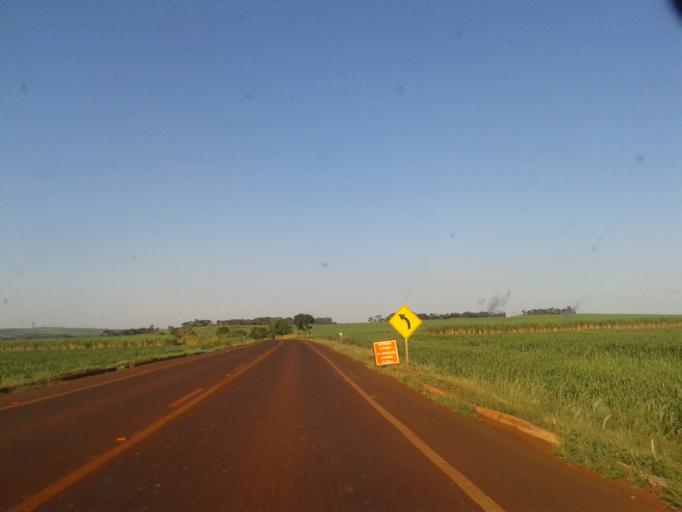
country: BR
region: Minas Gerais
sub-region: Capinopolis
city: Capinopolis
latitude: -18.6975
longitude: -49.6352
